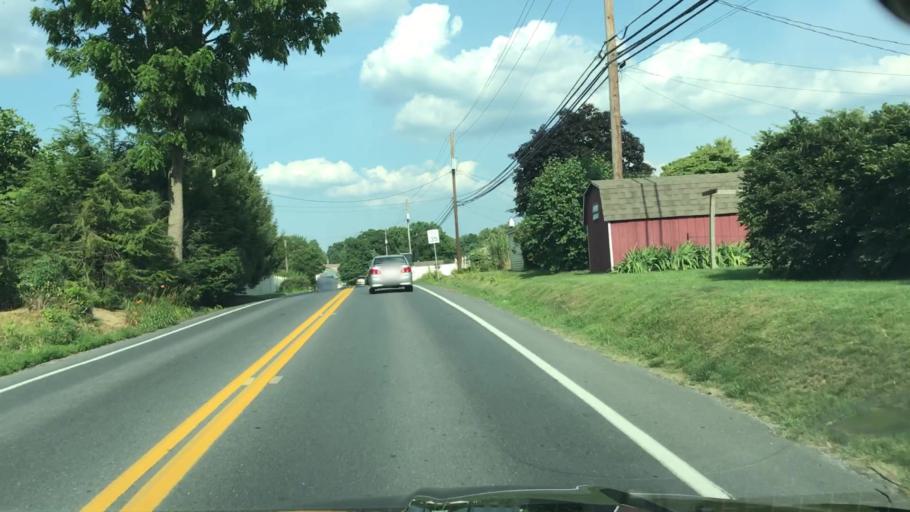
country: US
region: Pennsylvania
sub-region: Cumberland County
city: Mechanicsburg
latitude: 40.1623
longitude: -77.0075
